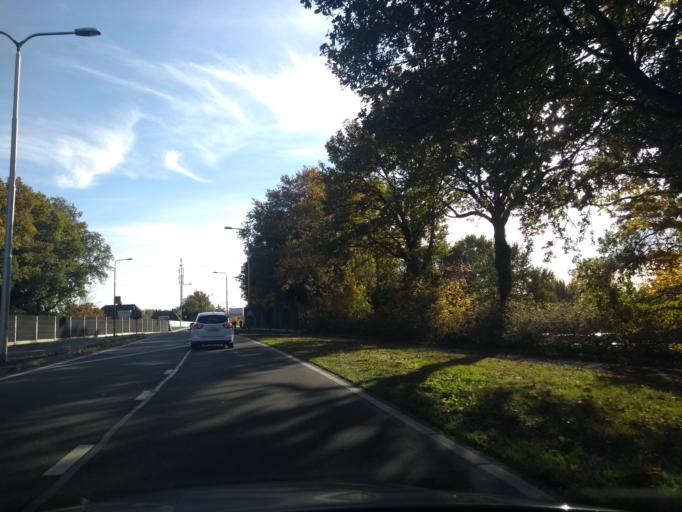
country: NL
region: Overijssel
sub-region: Gemeente Almelo
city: Almelo
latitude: 52.3665
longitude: 6.6714
